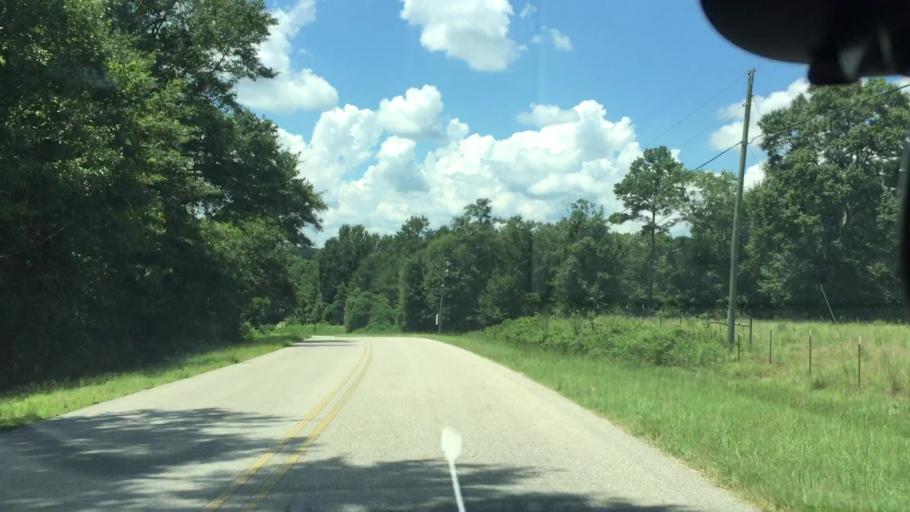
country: US
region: Alabama
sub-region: Pike County
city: Troy
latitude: 31.7493
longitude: -85.9765
